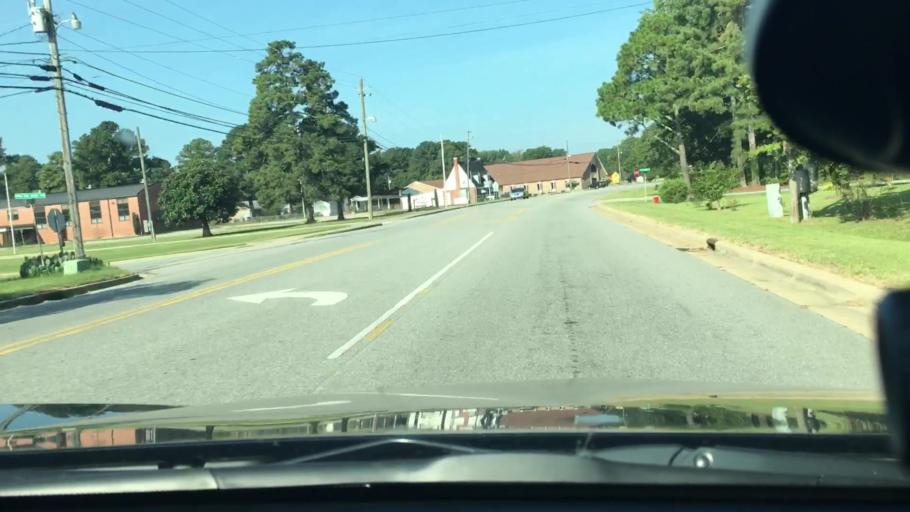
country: US
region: North Carolina
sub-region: Edgecombe County
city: Pinetops
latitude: 35.7889
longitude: -77.6299
